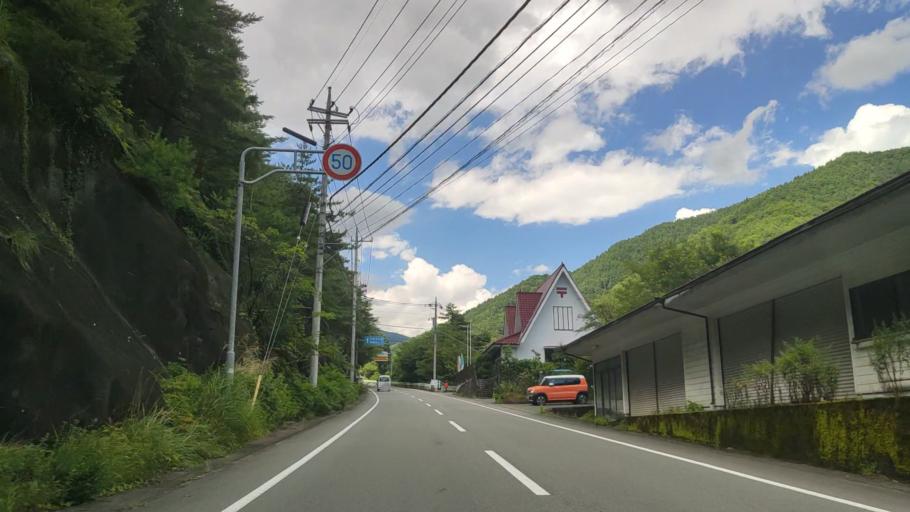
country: JP
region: Yamanashi
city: Enzan
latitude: 35.7748
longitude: 138.7387
